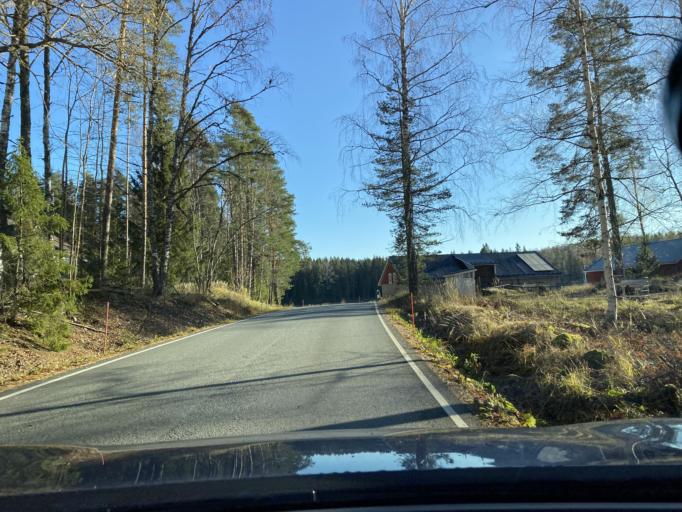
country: FI
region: Haeme
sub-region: Haemeenlinna
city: Kalvola
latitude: 61.0269
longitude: 24.1705
